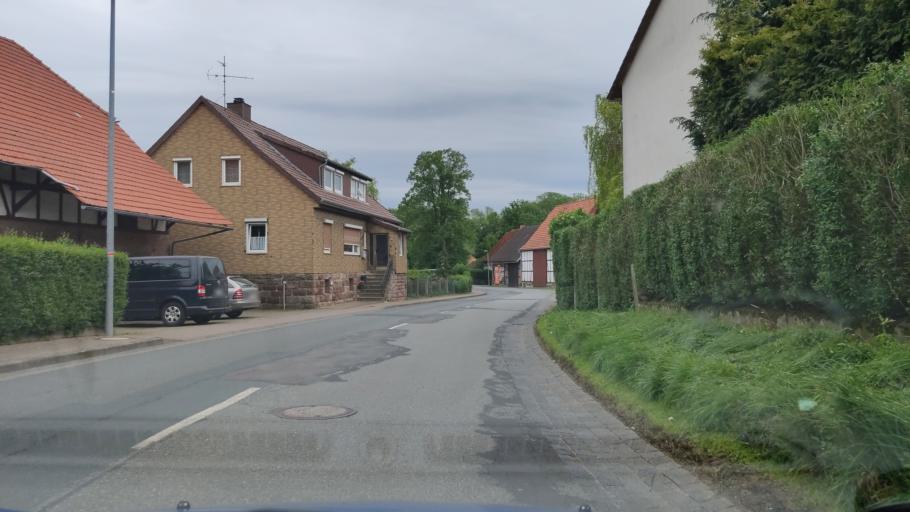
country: DE
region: Lower Saxony
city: Hardegsen
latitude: 51.6904
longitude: 9.8036
